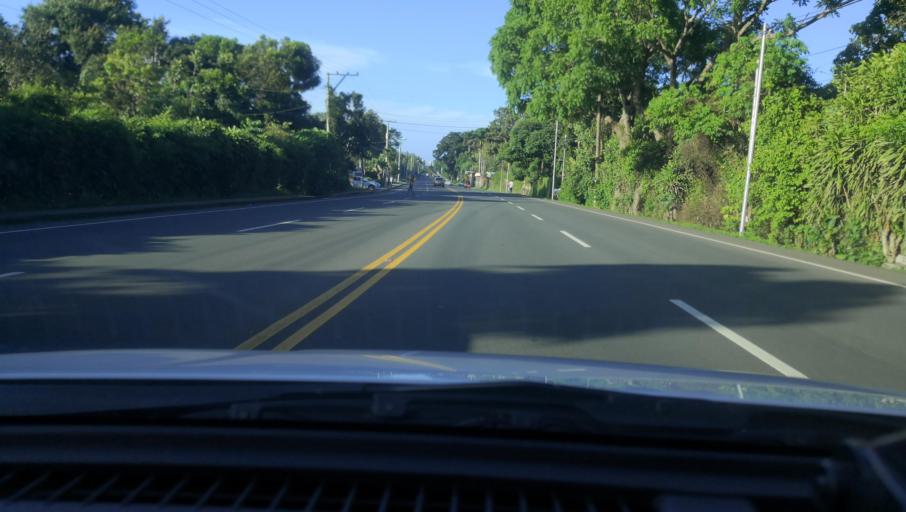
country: NI
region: Carazo
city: Diriamba
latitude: 11.8735
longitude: -86.2385
